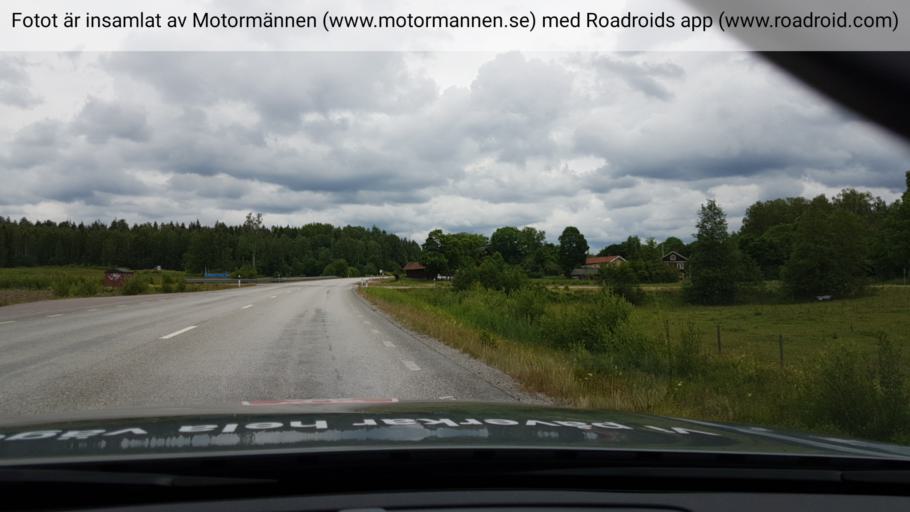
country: SE
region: OErebro
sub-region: Lindesbergs Kommun
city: Lindesberg
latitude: 59.6447
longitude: 15.2343
